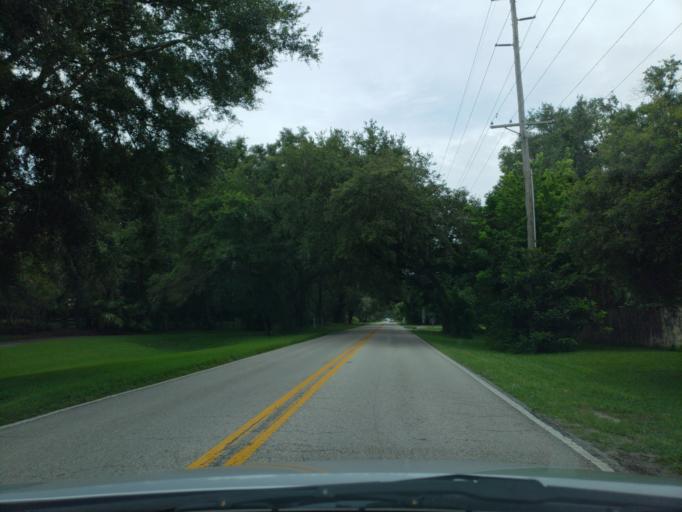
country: US
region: Florida
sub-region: Hillsborough County
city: Lutz
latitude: 28.1284
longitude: -82.4306
